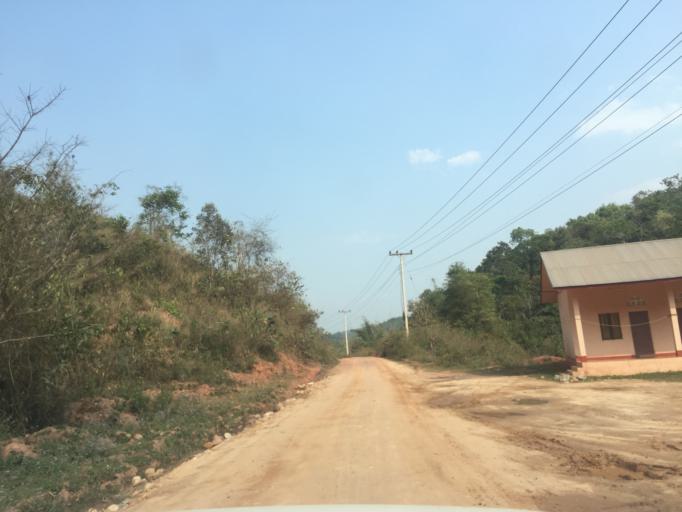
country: LA
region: Oudomxai
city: Muang La
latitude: 21.0741
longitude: 101.8231
